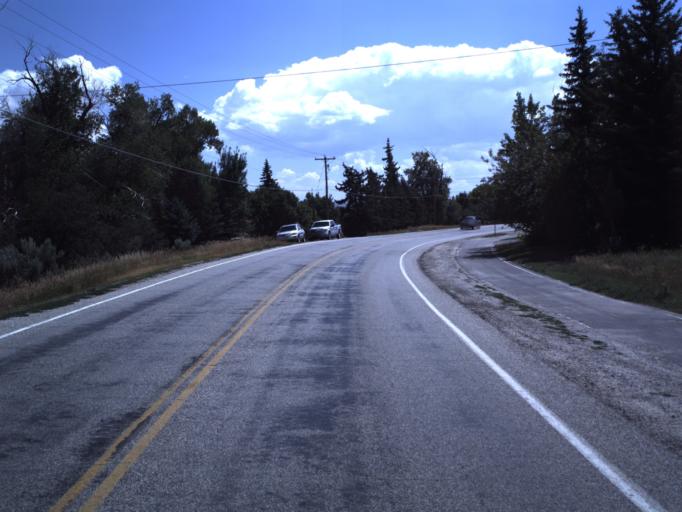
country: US
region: Idaho
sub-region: Bear Lake County
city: Paris
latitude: 41.9535
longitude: -111.3944
